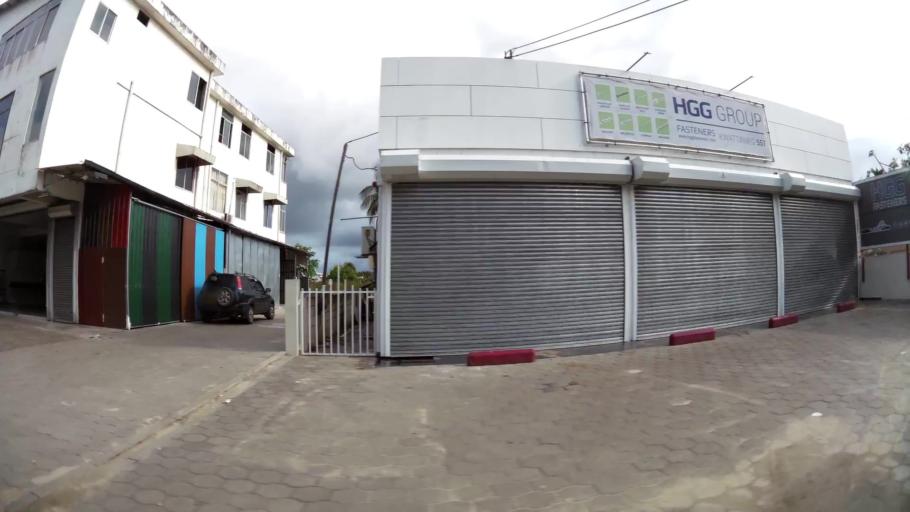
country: SR
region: Paramaribo
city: Paramaribo
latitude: 5.8453
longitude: -55.2245
